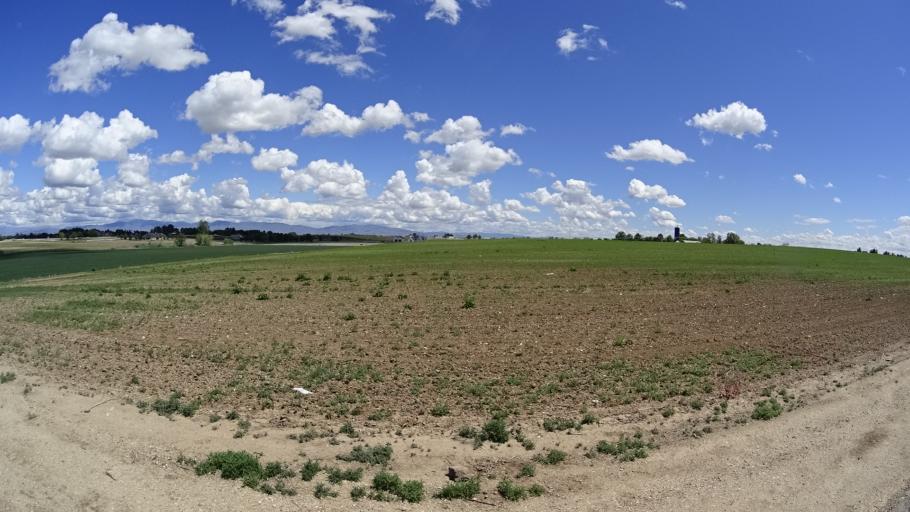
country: US
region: Idaho
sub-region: Ada County
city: Meridian
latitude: 43.5677
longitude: -116.4339
